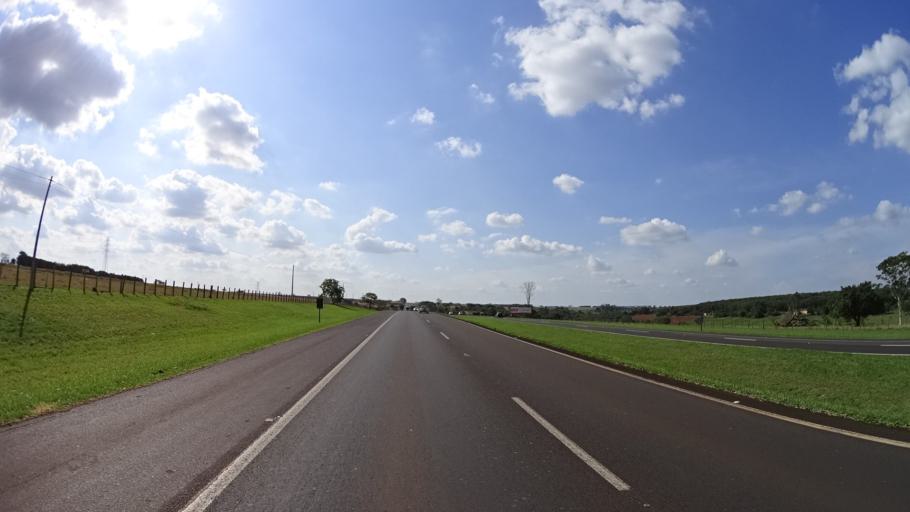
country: BR
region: Sao Paulo
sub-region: Guapiacu
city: Guapiacu
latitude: -20.9446
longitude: -49.2604
